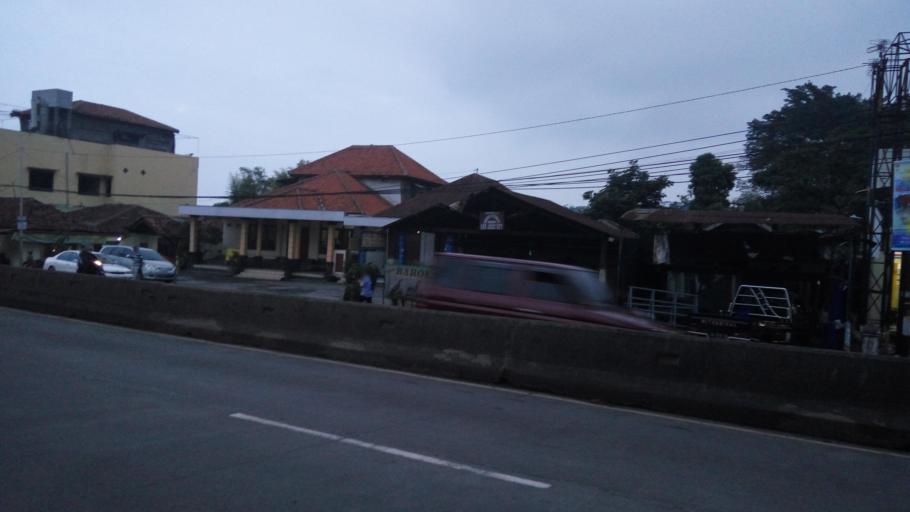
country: ID
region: Central Java
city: Ambarawa
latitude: -7.2120
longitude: 110.4246
